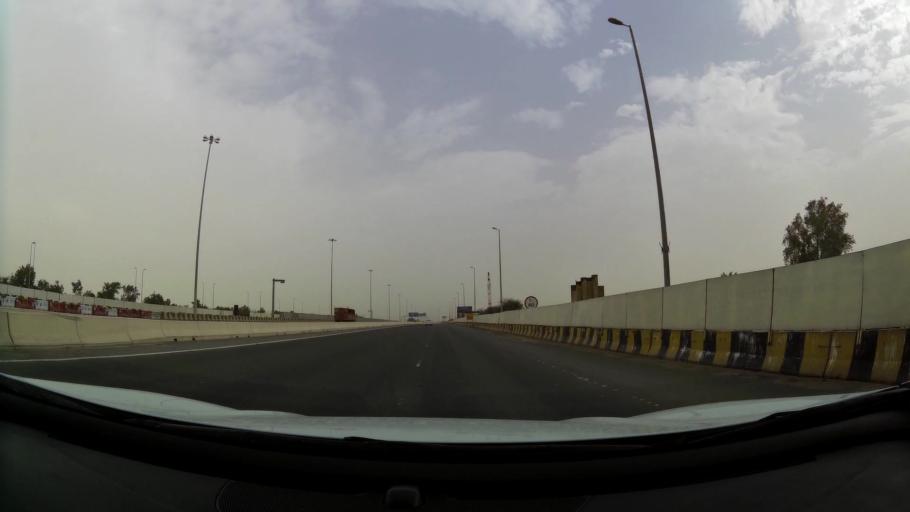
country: AE
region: Abu Dhabi
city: Abu Dhabi
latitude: 24.4751
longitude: 54.6369
